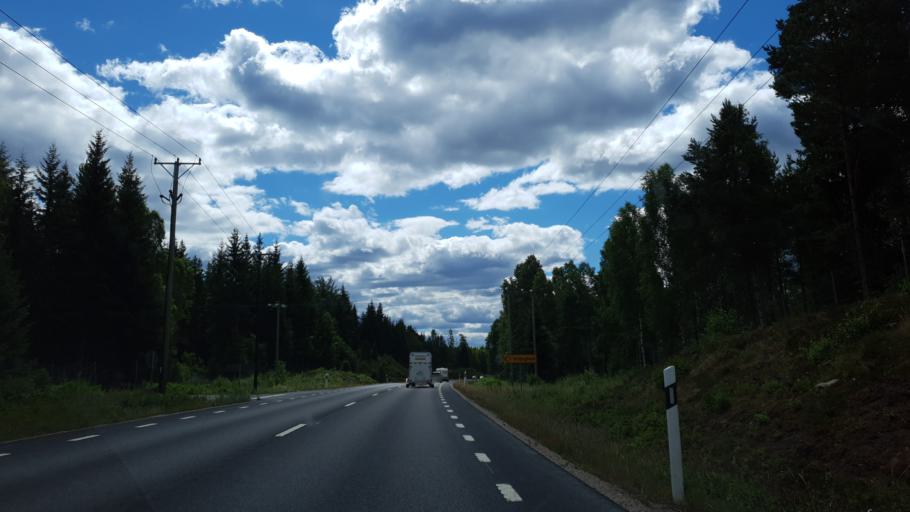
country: SE
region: Kronoberg
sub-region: Vaxjo Kommun
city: Braas
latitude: 57.2127
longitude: 15.1512
